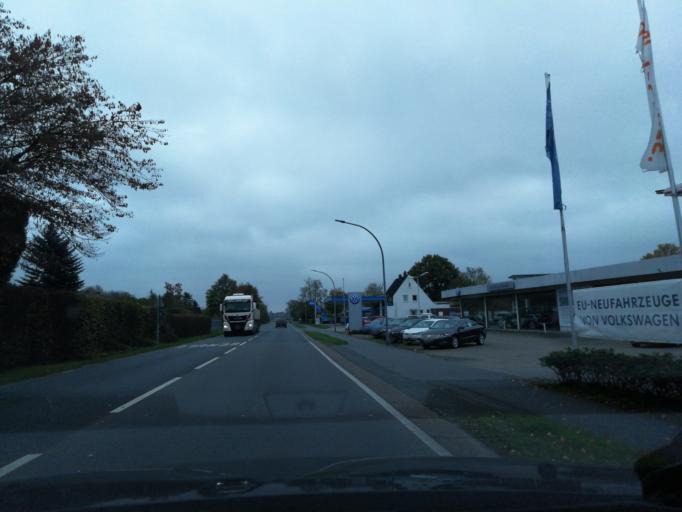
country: DE
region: Lower Saxony
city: Schortens
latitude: 53.5430
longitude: 7.9519
